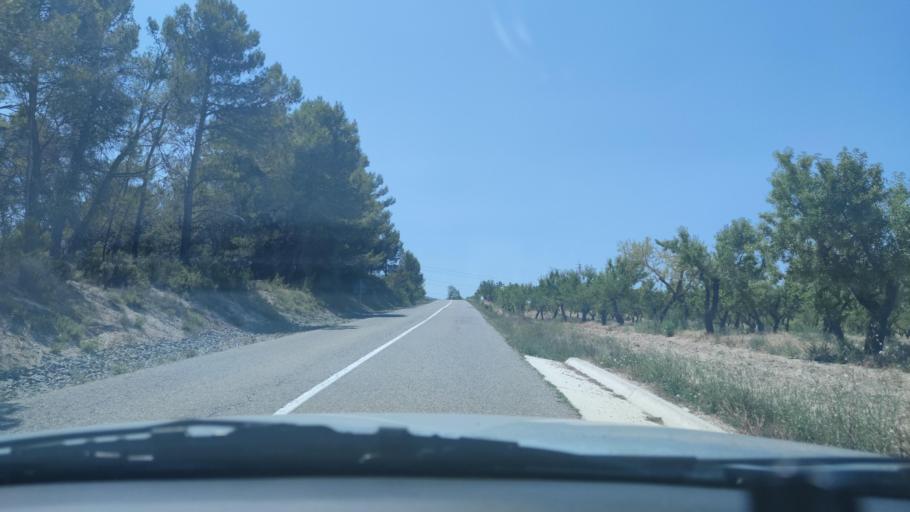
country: ES
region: Catalonia
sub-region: Provincia de Lleida
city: Vinaixa
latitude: 41.4070
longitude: 0.9582
